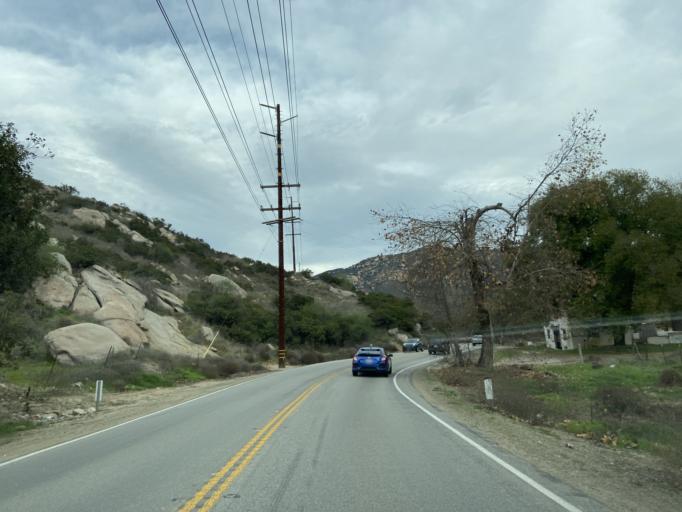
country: US
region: California
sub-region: San Diego County
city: Rainbow
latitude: 33.3441
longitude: -117.1261
